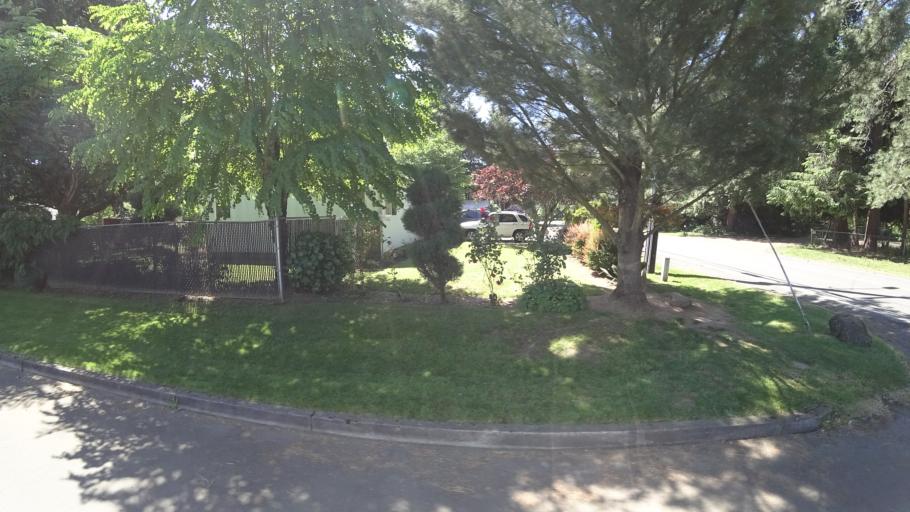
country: US
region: Oregon
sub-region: Clackamas County
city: Happy Valley
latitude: 45.4741
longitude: -122.5260
